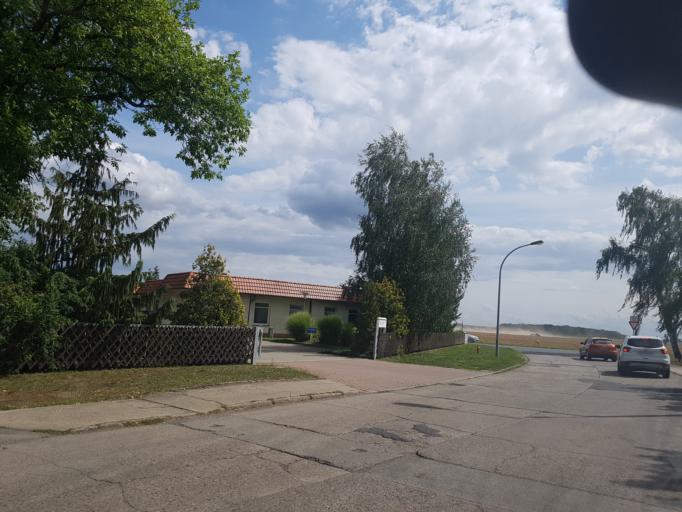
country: DE
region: Brandenburg
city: Herzberg
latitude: 51.6948
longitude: 13.2566
